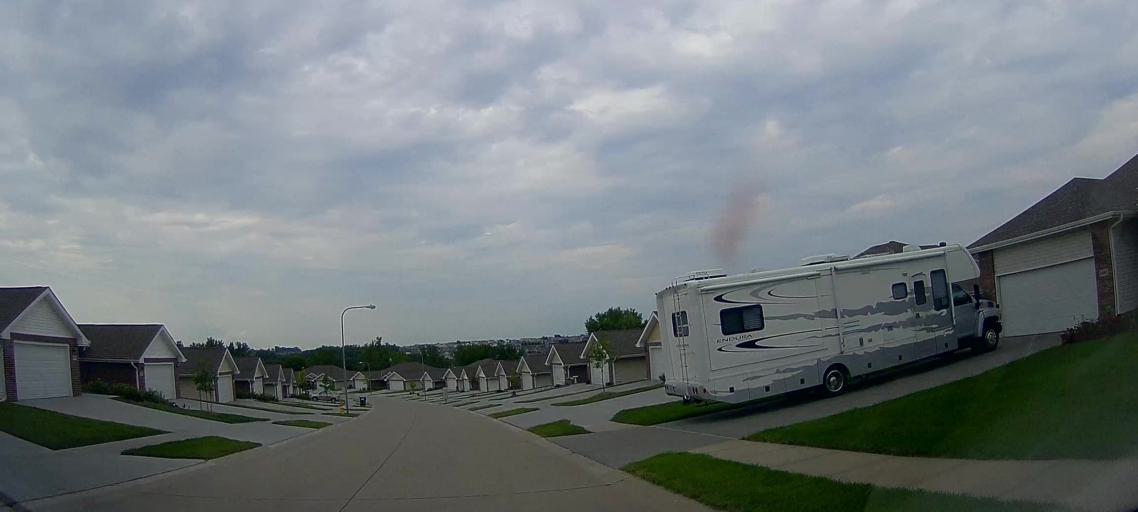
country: US
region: Nebraska
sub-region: Douglas County
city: Ralston
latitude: 41.3120
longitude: -96.0558
